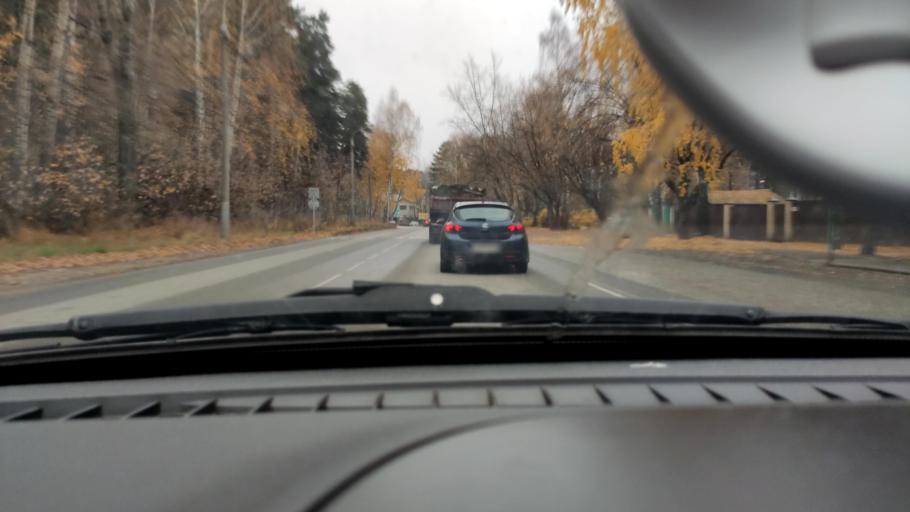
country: RU
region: Perm
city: Kondratovo
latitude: 58.0199
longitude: 56.0086
